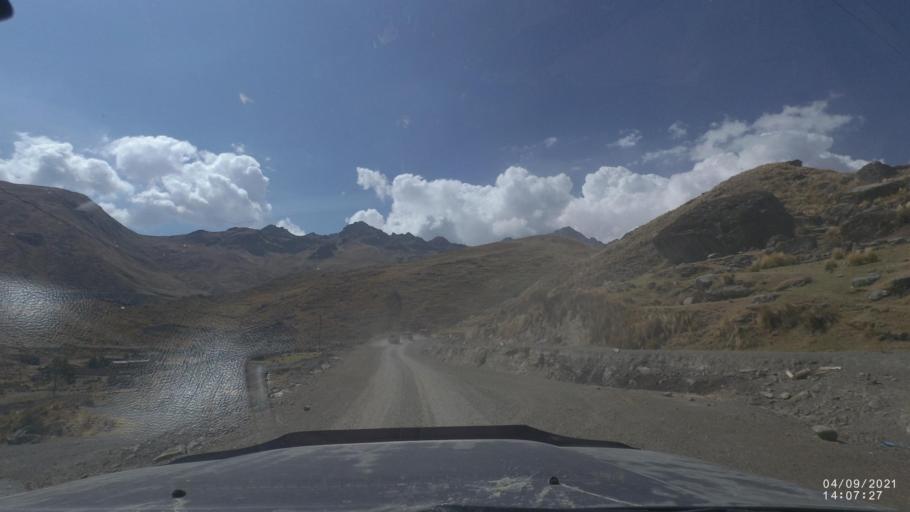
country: BO
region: Cochabamba
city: Sipe Sipe
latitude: -17.2274
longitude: -66.4673
